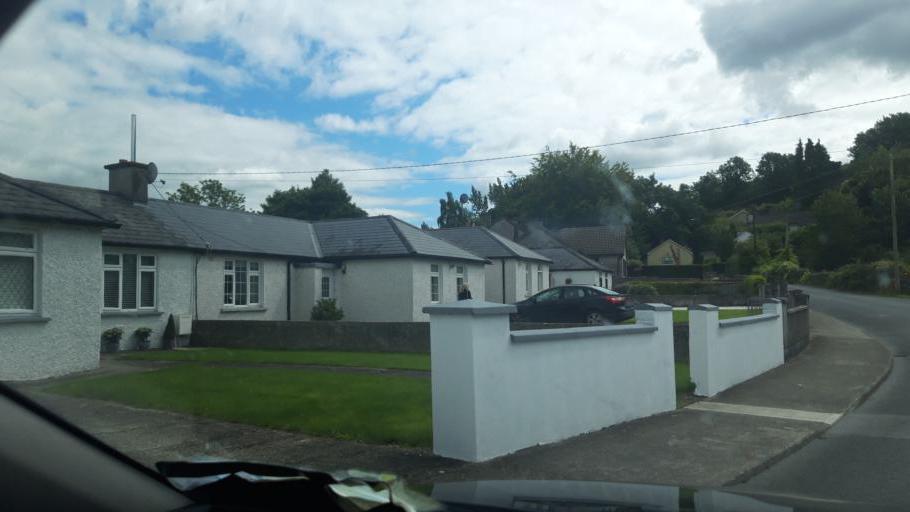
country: IE
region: Munster
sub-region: South Tipperary
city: Cluain Meala
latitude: 52.3479
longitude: -7.7032
